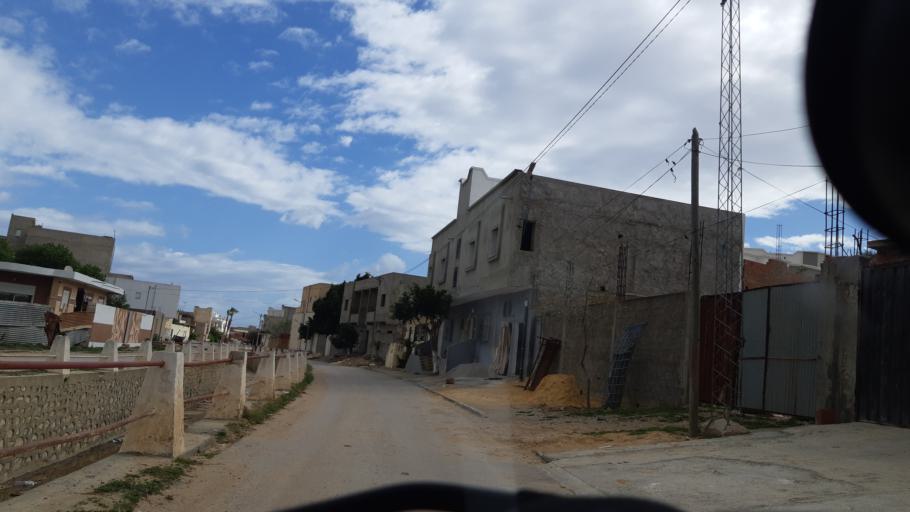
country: TN
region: Susah
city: Akouda
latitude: 35.8668
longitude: 10.5336
